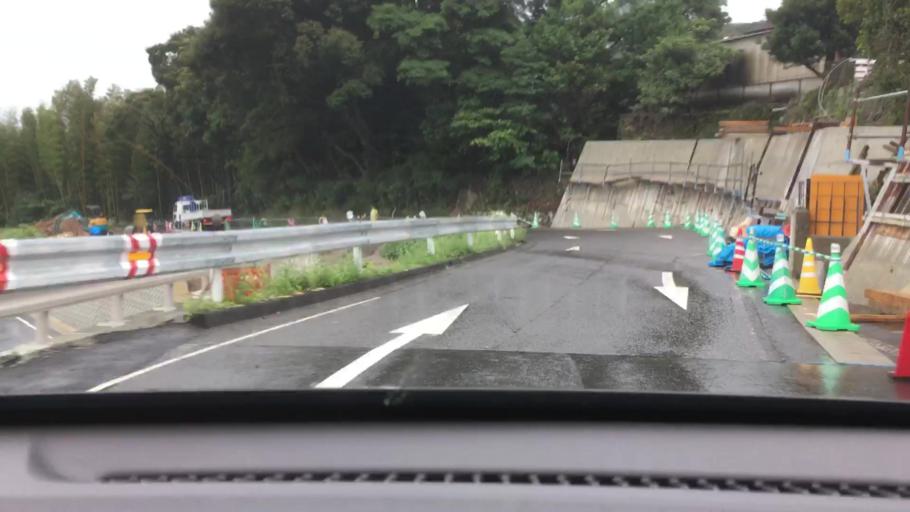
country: JP
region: Nagasaki
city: Togitsu
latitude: 32.8682
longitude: 129.7669
